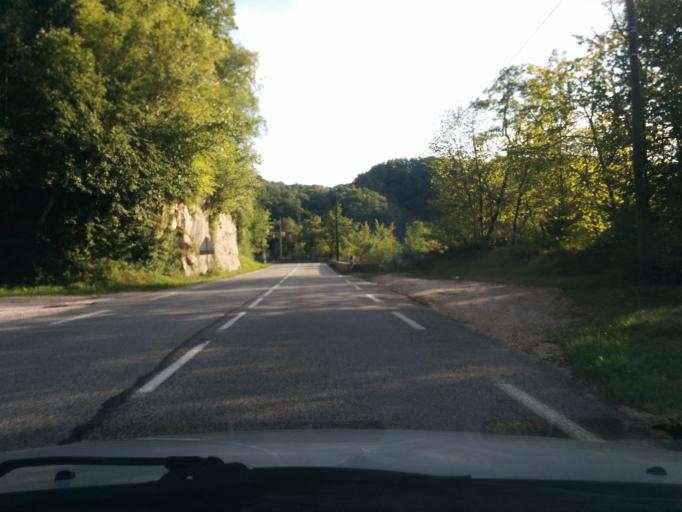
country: FR
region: Rhone-Alpes
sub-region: Departement de la Savoie
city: Saint-Beron
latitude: 45.4850
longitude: 5.7212
